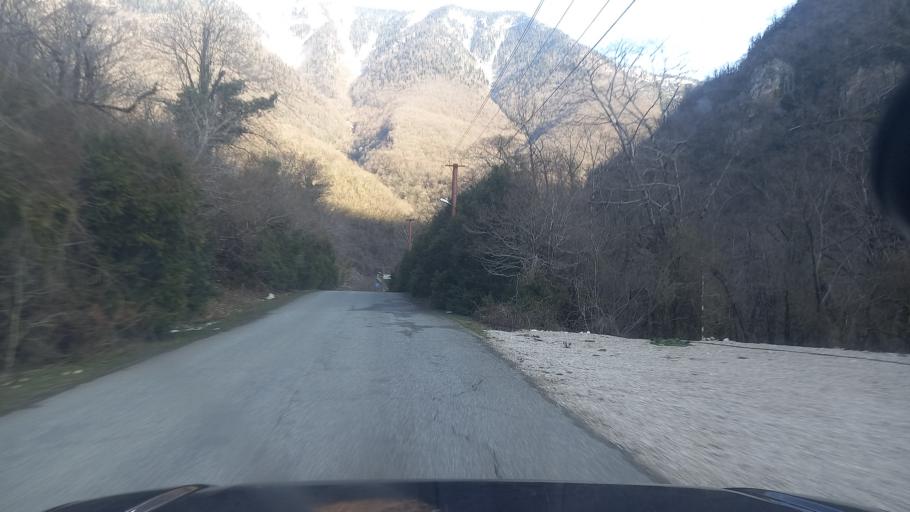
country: GE
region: Abkhazia
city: Gagra
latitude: 43.3456
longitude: 40.4128
